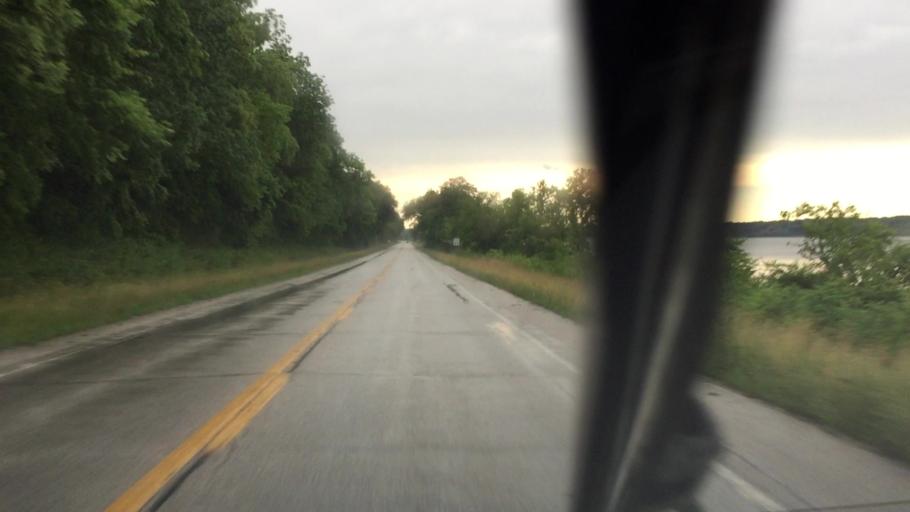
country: US
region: Iowa
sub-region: Lee County
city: Keokuk
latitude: 40.4605
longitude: -91.3649
